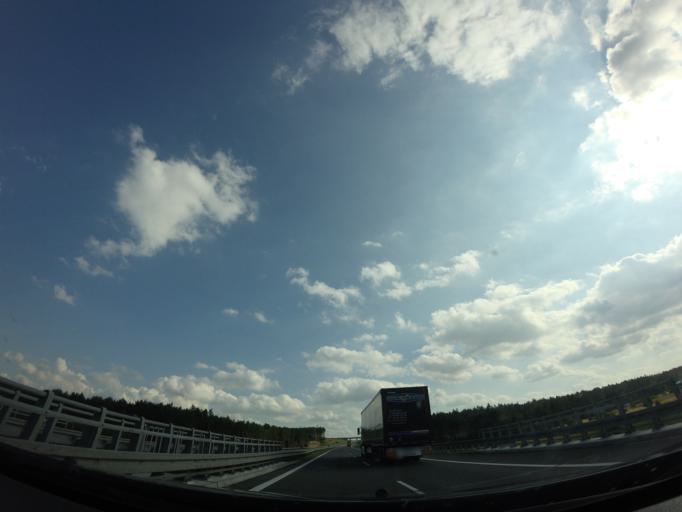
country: PL
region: Lubusz
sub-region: Powiat swiebodzinski
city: Swiebodzin
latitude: 52.3307
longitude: 15.5557
